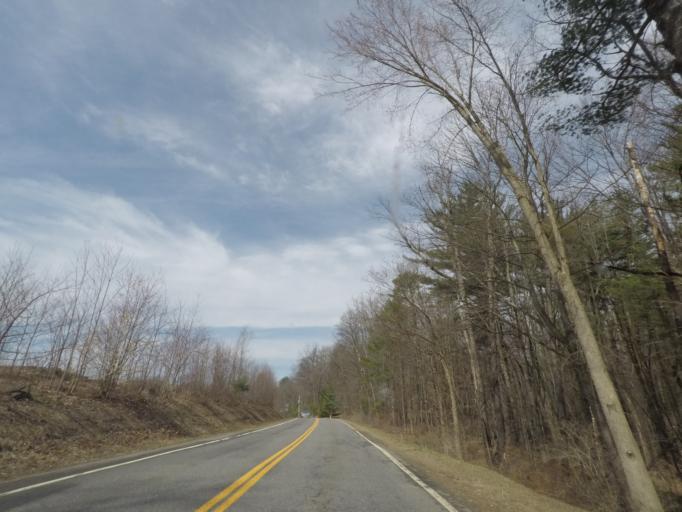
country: US
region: New York
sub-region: Saratoga County
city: Country Knolls
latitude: 42.9060
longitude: -73.7560
